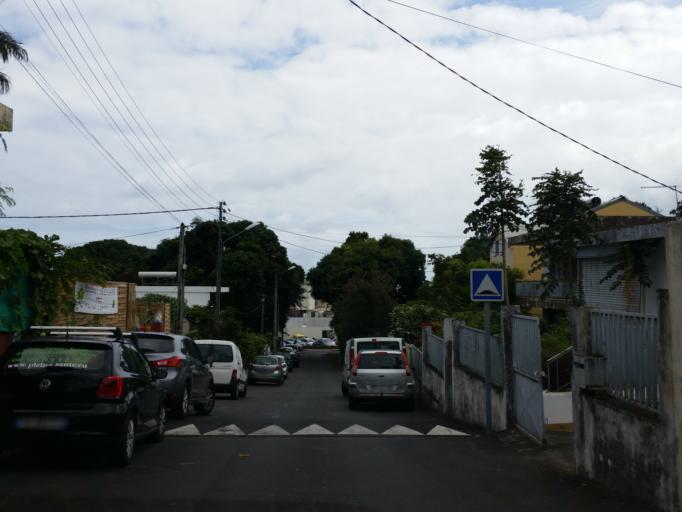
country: RE
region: Reunion
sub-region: Reunion
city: Saint-Denis
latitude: -20.8978
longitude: 55.4575
